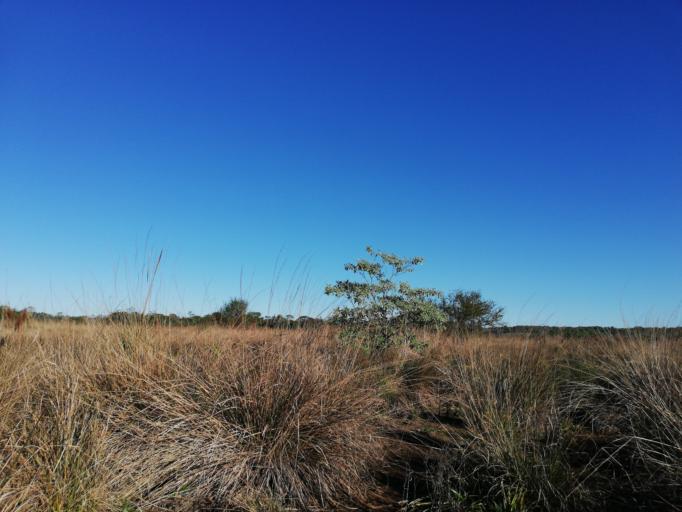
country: AR
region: Misiones
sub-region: Departamento de Candelaria
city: Candelaria
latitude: -27.4979
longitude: -55.7732
